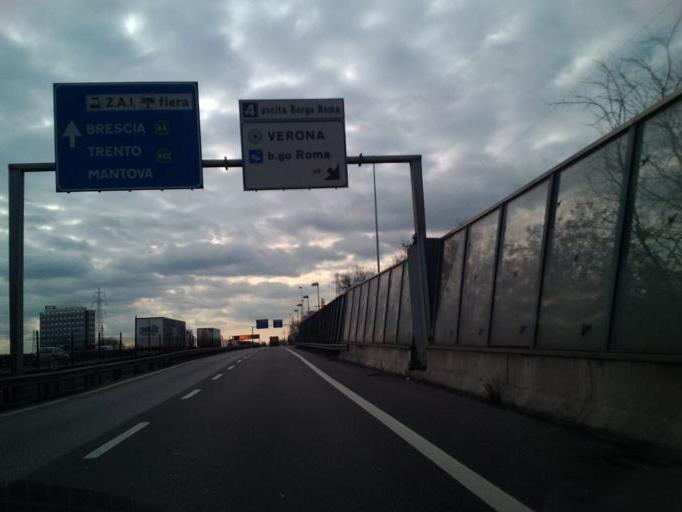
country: IT
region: Veneto
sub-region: Provincia di Verona
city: Marchesino-Bovo
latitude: 45.3988
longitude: 10.9947
